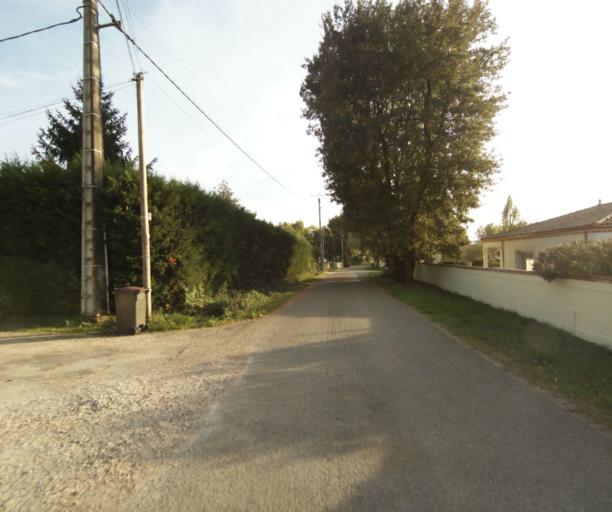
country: FR
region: Midi-Pyrenees
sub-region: Departement du Tarn-et-Garonne
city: Labastide-Saint-Pierre
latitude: 43.9171
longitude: 1.3507
